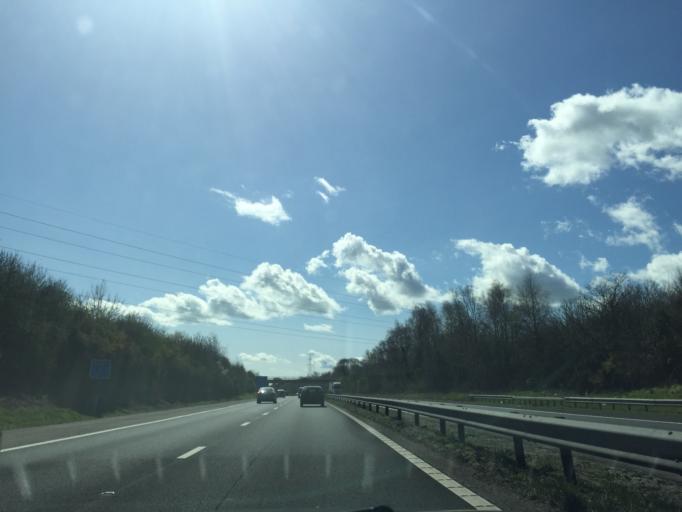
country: GB
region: England
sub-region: Hampshire
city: Waterlooville
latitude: 50.8670
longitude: -1.0164
